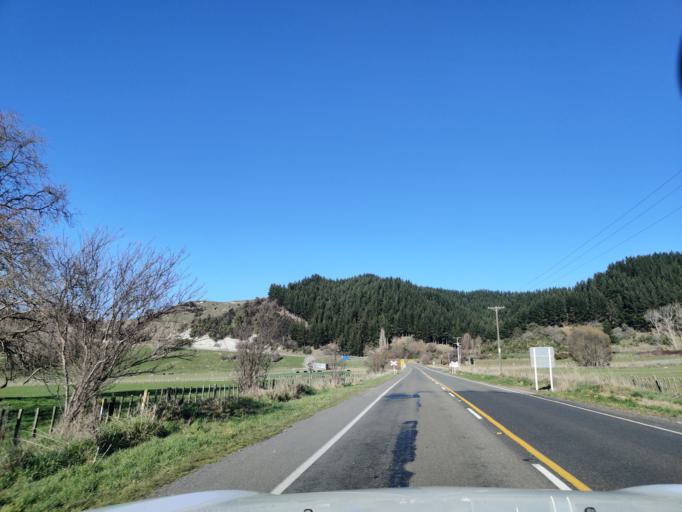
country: NZ
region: Manawatu-Wanganui
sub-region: Ruapehu District
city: Waiouru
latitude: -39.8193
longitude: 175.7789
